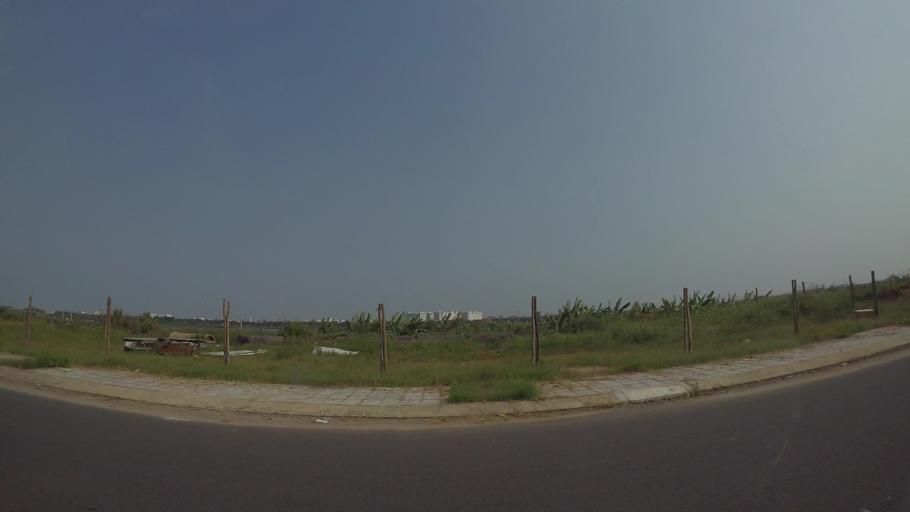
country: VN
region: Da Nang
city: Cam Le
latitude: 16.0061
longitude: 108.1991
